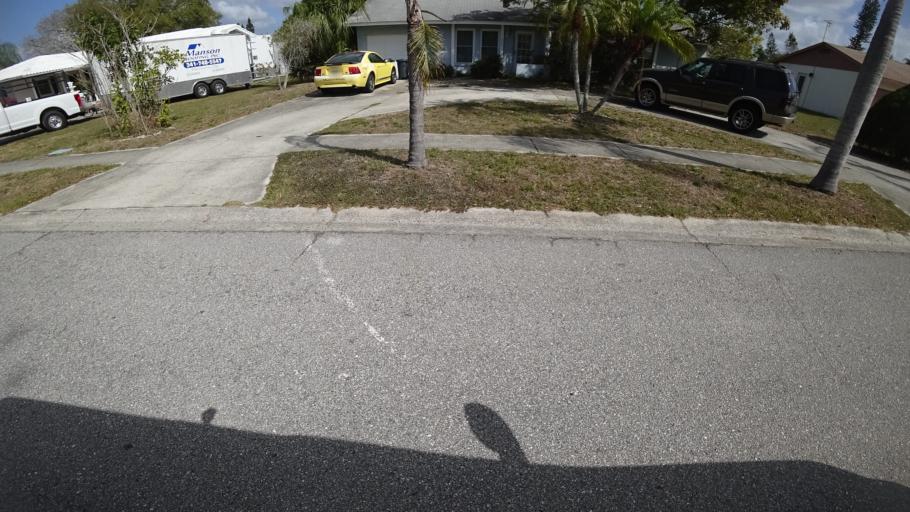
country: US
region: Florida
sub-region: Manatee County
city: Whitfield
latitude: 27.4098
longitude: -82.5567
